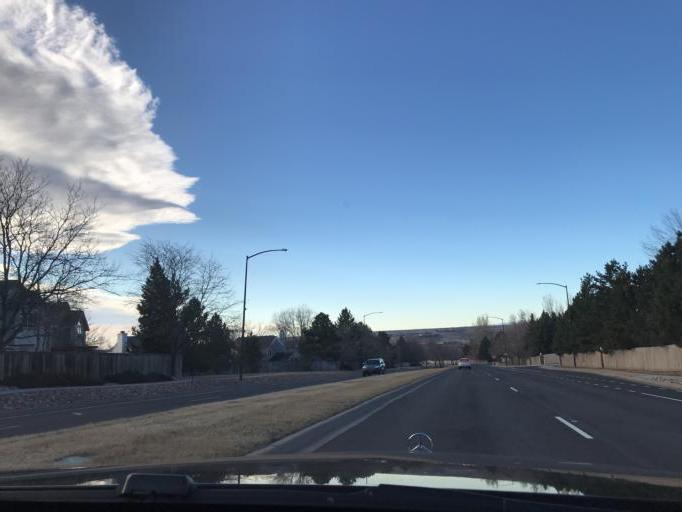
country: US
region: Colorado
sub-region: Boulder County
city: Superior
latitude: 39.9773
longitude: -105.1659
